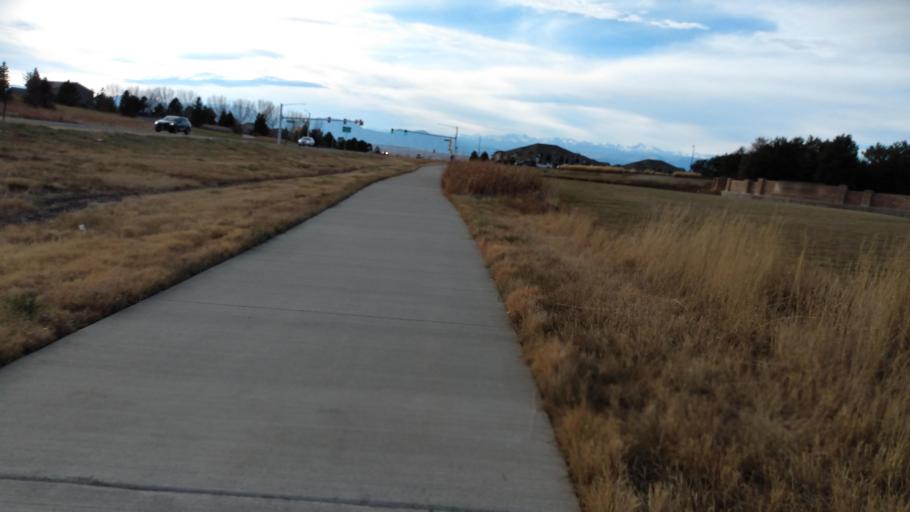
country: US
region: Colorado
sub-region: Boulder County
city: Erie
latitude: 40.0006
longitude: -105.0246
